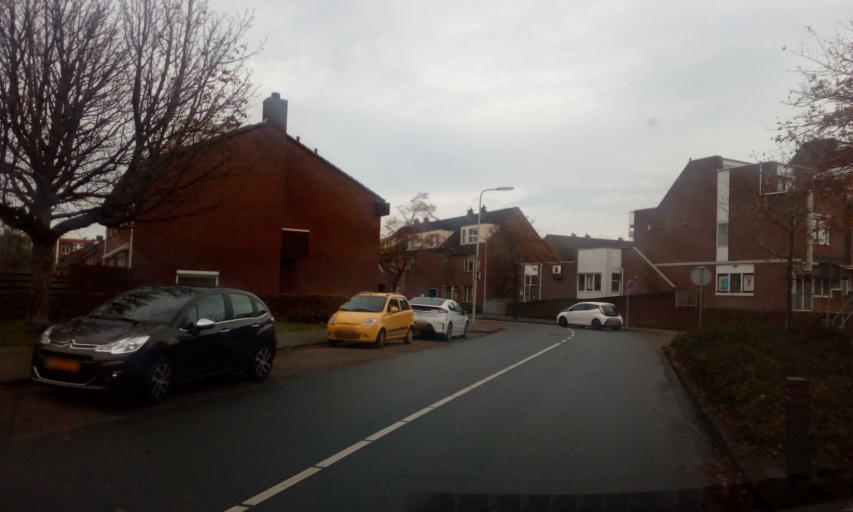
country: NL
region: South Holland
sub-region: Gemeente Westland
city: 's-Gravenzande
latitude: 52.0019
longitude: 4.1579
